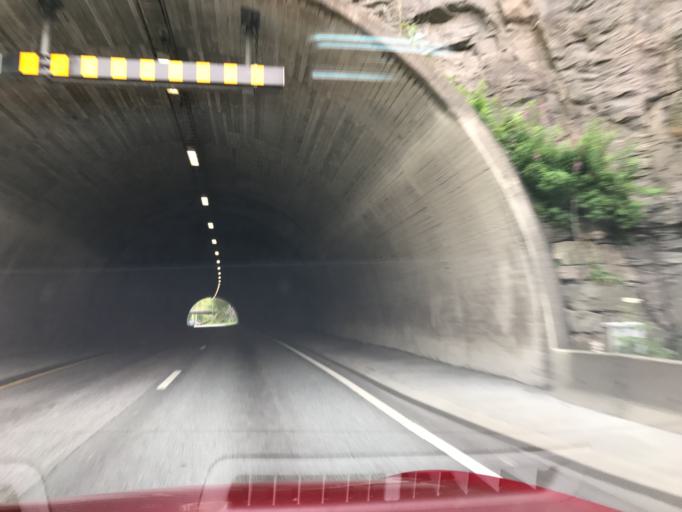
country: NO
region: Hordaland
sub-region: Bergen
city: Bergen
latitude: 60.4400
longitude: 5.3259
